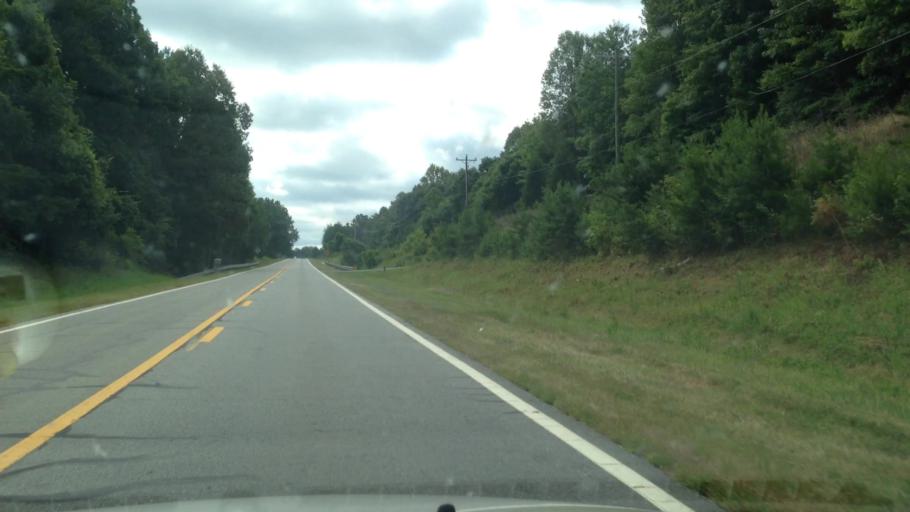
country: US
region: North Carolina
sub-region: Rockingham County
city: Wentworth
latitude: 36.3793
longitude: -79.8606
